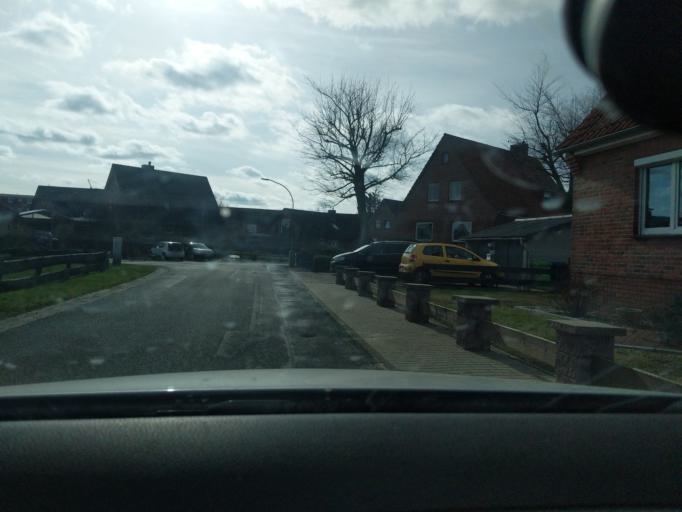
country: DE
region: Lower Saxony
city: Drochtersen
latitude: 53.7101
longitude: 9.3916
